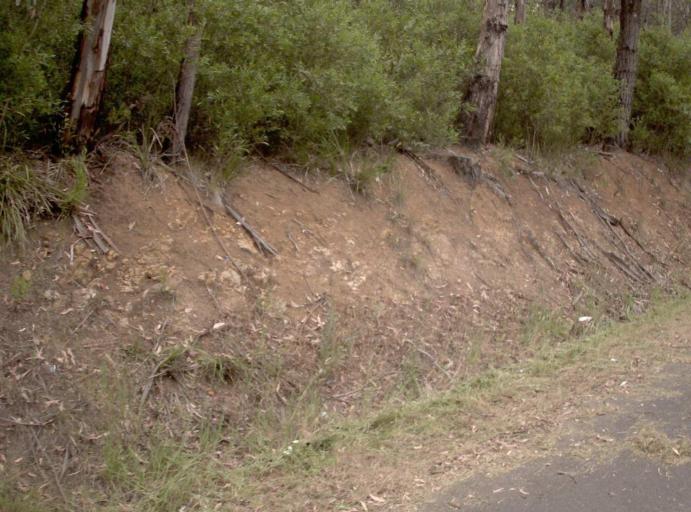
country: AU
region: Victoria
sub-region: Latrobe
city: Moe
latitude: -38.3108
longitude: 146.2689
